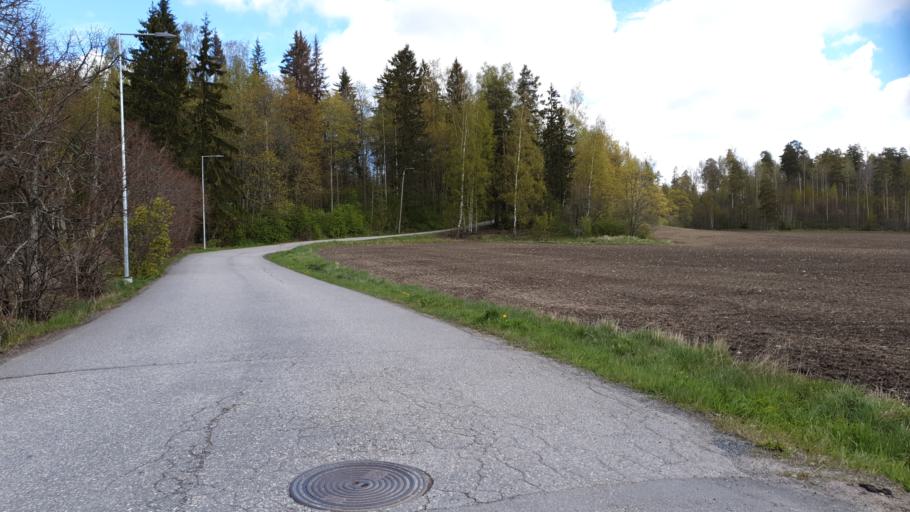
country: FI
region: Uusimaa
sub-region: Helsinki
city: Nurmijaervi
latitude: 60.3443
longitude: 24.8376
